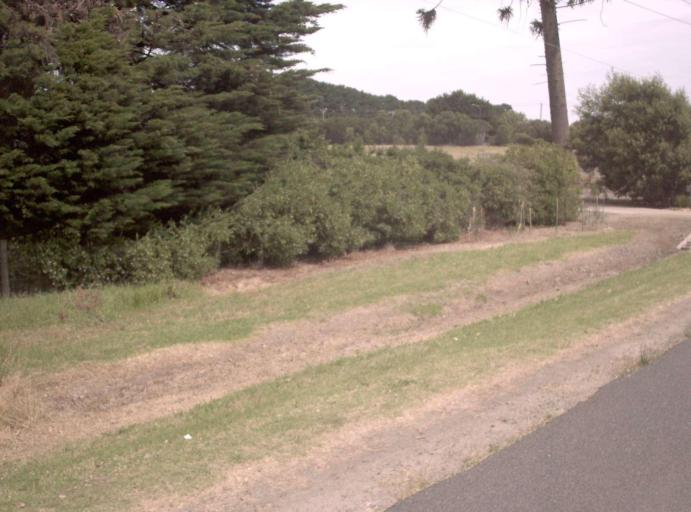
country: AU
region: Victoria
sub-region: Mornington Peninsula
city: Moorooduc
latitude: -38.2425
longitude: 145.0848
